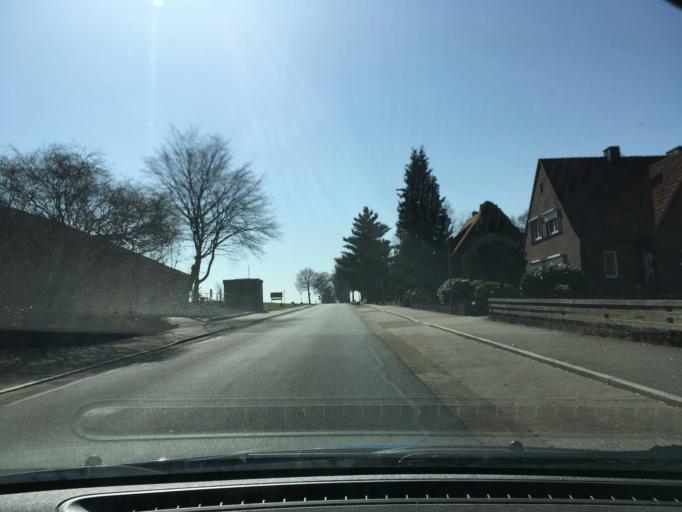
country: DE
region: Lower Saxony
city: Wriedel
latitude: 53.0286
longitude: 10.2936
